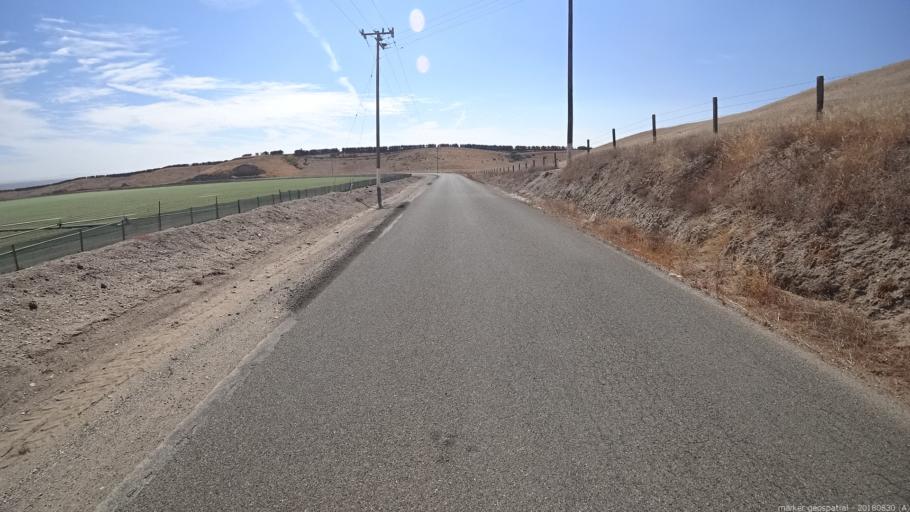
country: US
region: California
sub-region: Monterey County
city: King City
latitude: 36.1080
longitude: -121.0524
